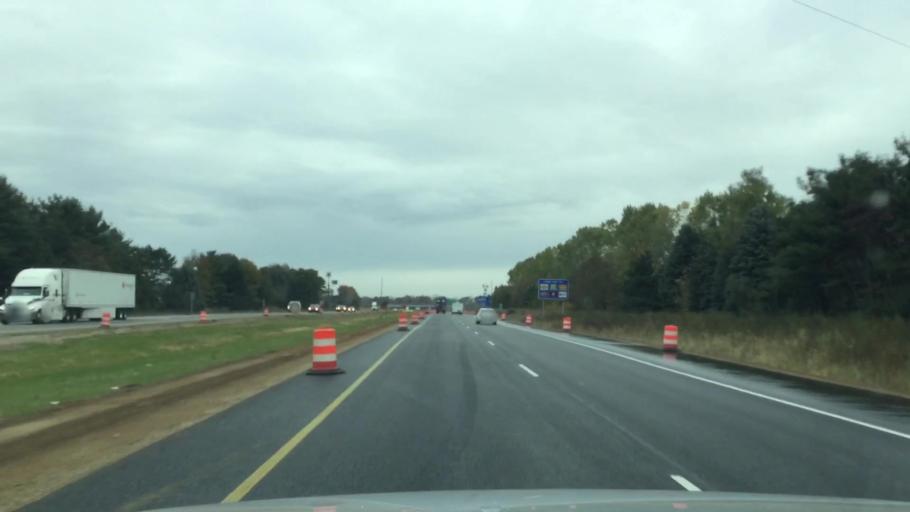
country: US
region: Michigan
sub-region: Calhoun County
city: Marshall
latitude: 42.2888
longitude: -84.9554
